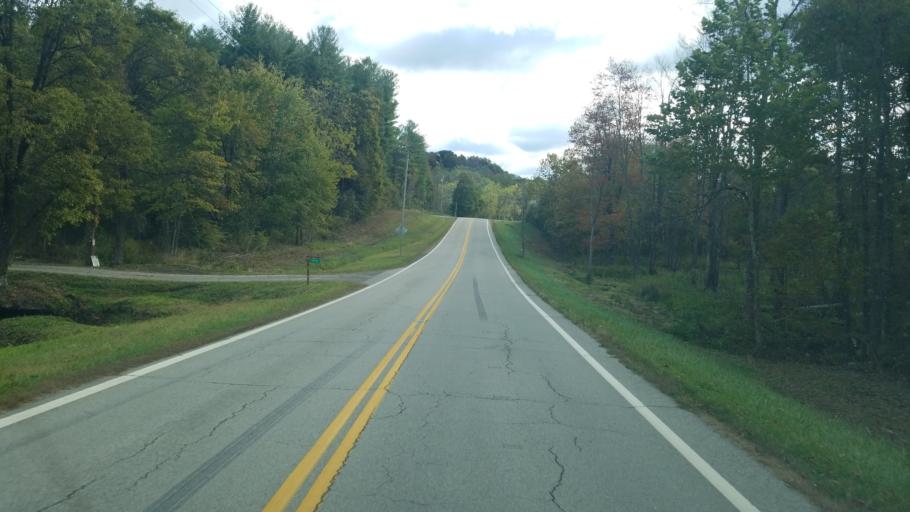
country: US
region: Ohio
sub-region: Vinton County
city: McArthur
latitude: 39.1645
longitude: -82.4521
